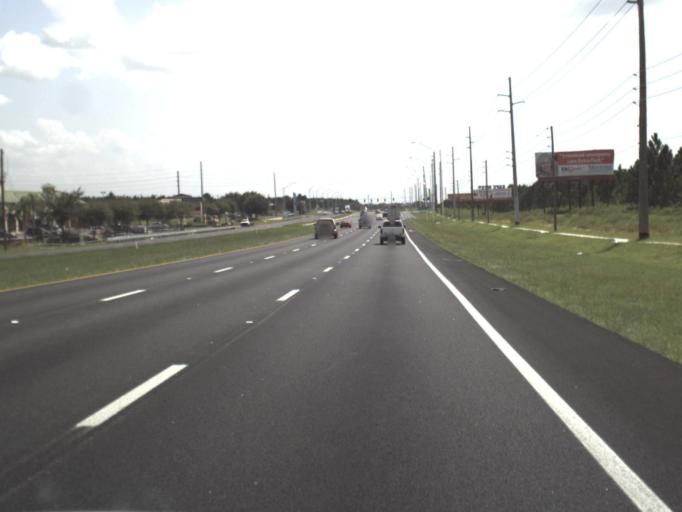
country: US
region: Florida
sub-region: Lake County
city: Four Corners
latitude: 28.2584
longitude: -81.6594
